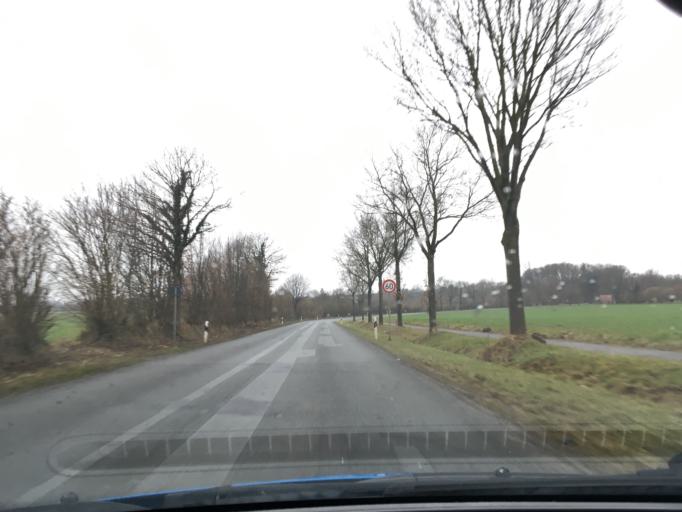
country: DE
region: Schleswig-Holstein
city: Breitenfelde
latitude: 53.5971
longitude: 10.6421
